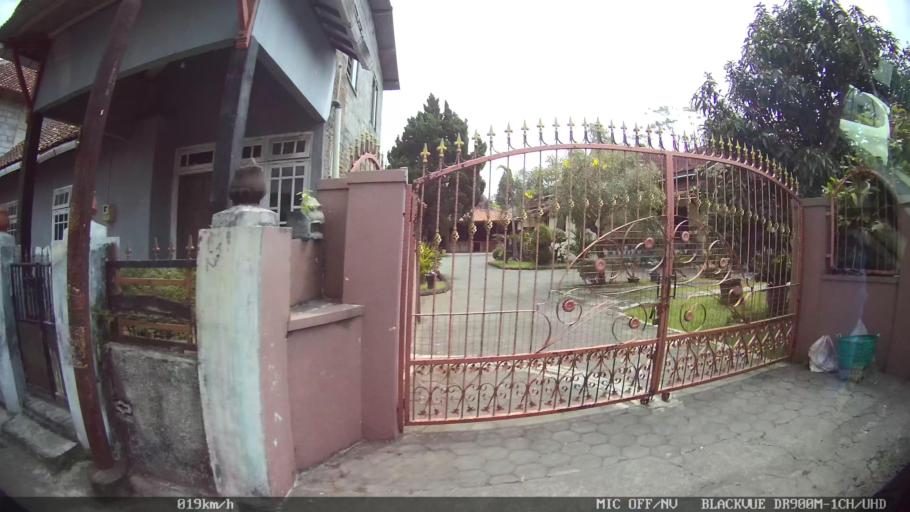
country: ID
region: Daerah Istimewa Yogyakarta
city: Kasihan
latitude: -7.8191
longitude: 110.3401
